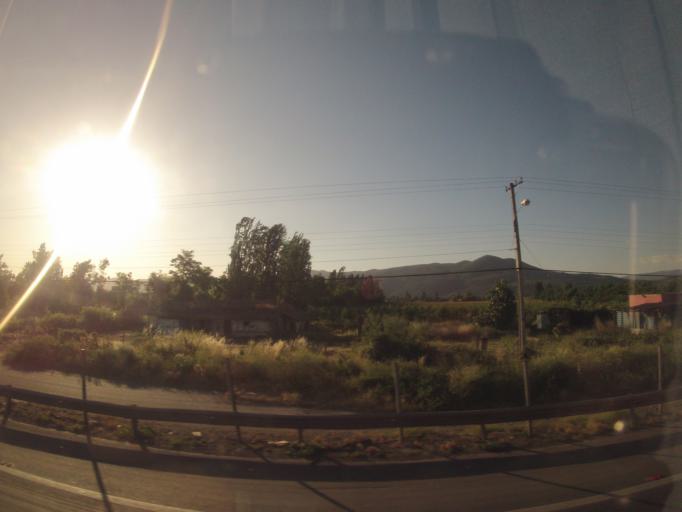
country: CL
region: O'Higgins
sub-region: Provincia de Colchagua
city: Chimbarongo
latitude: -34.7063
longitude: -71.0268
